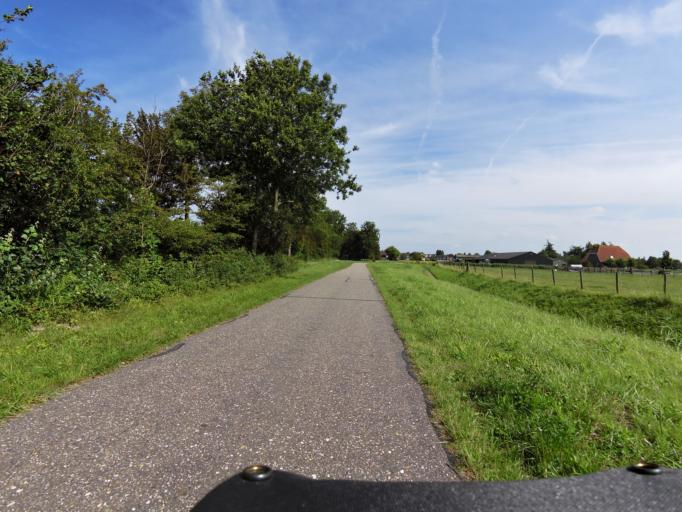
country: NL
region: South Holland
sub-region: Gemeente Goeree-Overflakkee
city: Middelharnis
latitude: 51.7544
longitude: 4.1413
